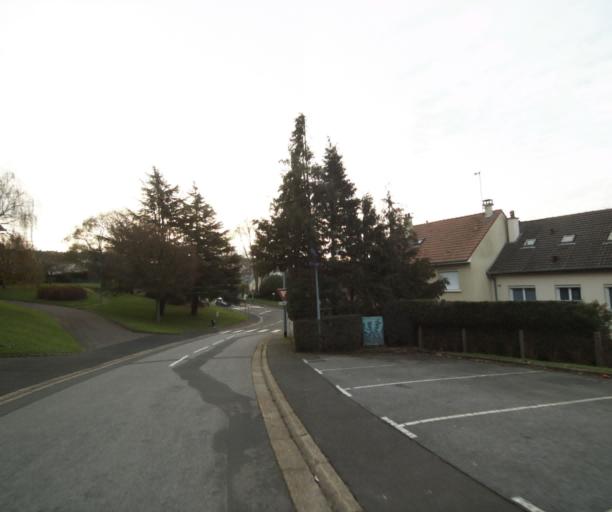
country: FR
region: Pays de la Loire
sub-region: Departement de la Sarthe
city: Coulaines
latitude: 48.0189
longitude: 0.2083
